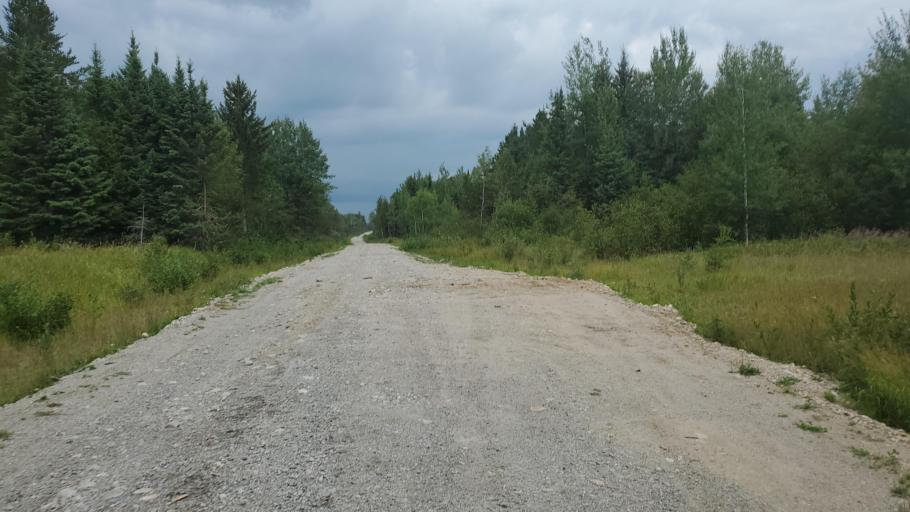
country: CA
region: Ontario
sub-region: Rainy River District
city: Atikokan
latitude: 49.5978
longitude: -91.3844
